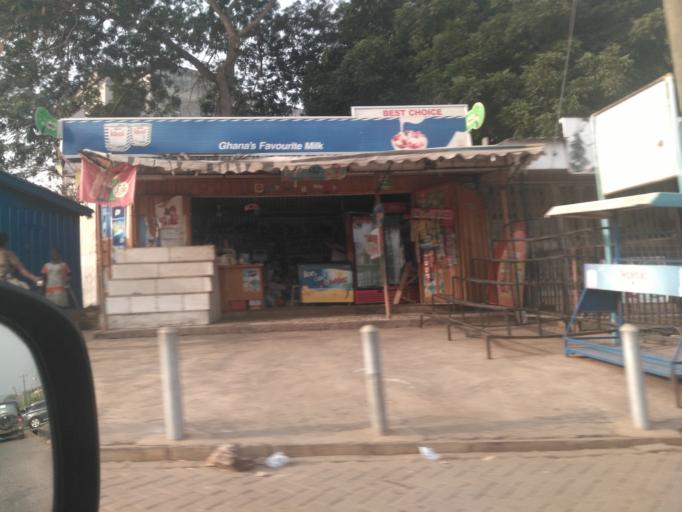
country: GH
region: Greater Accra
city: Accra
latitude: 5.6049
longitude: -0.1951
